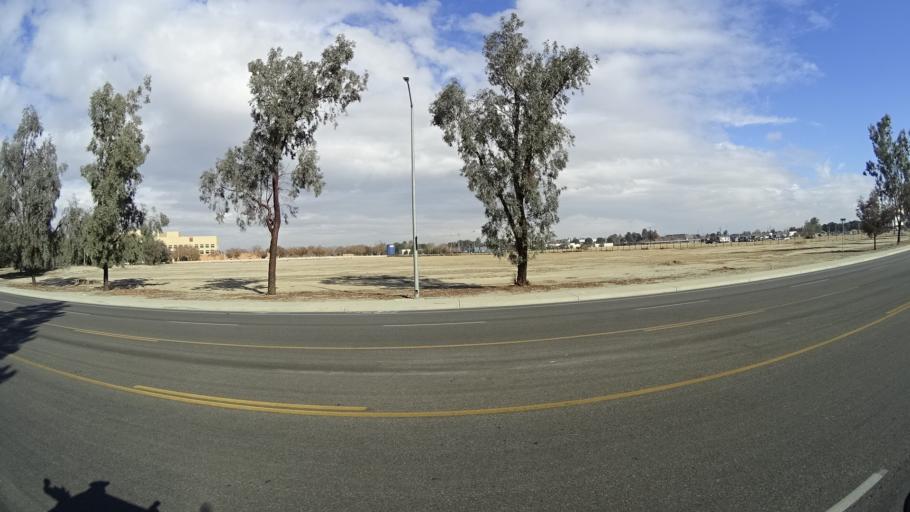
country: US
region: California
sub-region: Kern County
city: Greenacres
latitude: 35.3430
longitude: -119.1112
